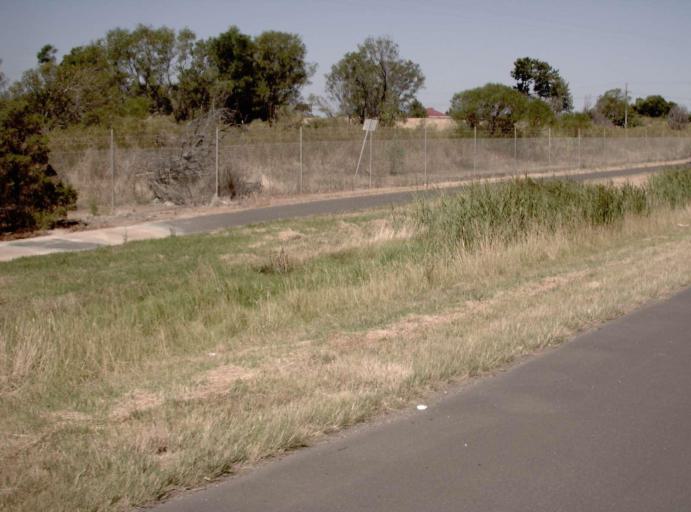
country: AU
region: Victoria
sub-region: Kingston
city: Dingley Village
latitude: -37.9788
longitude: 145.1422
